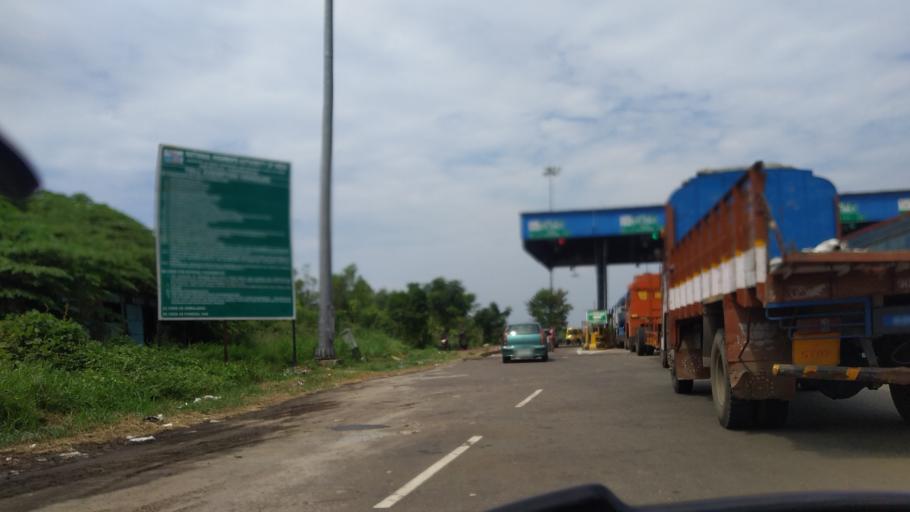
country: IN
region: Kerala
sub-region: Ernakulam
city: Elur
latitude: 10.0098
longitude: 76.2580
